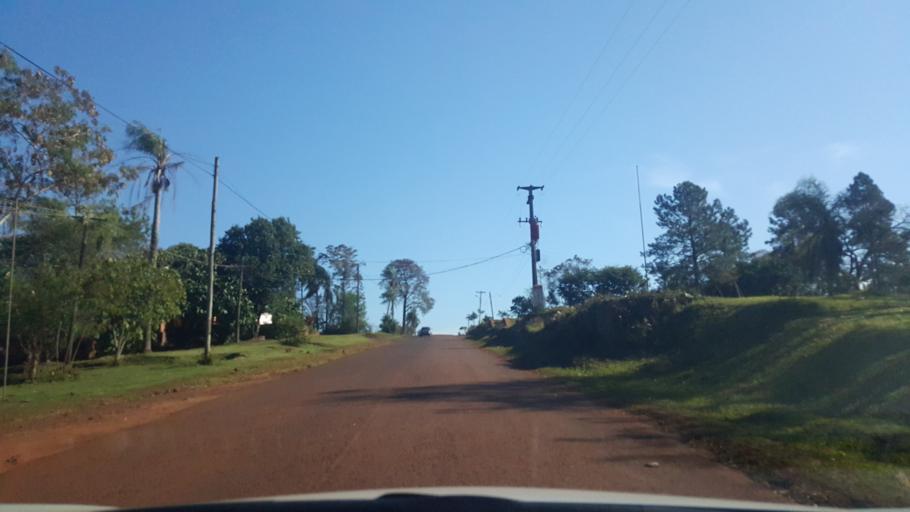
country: AR
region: Misiones
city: Santo Pipo
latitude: -27.1494
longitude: -55.3969
